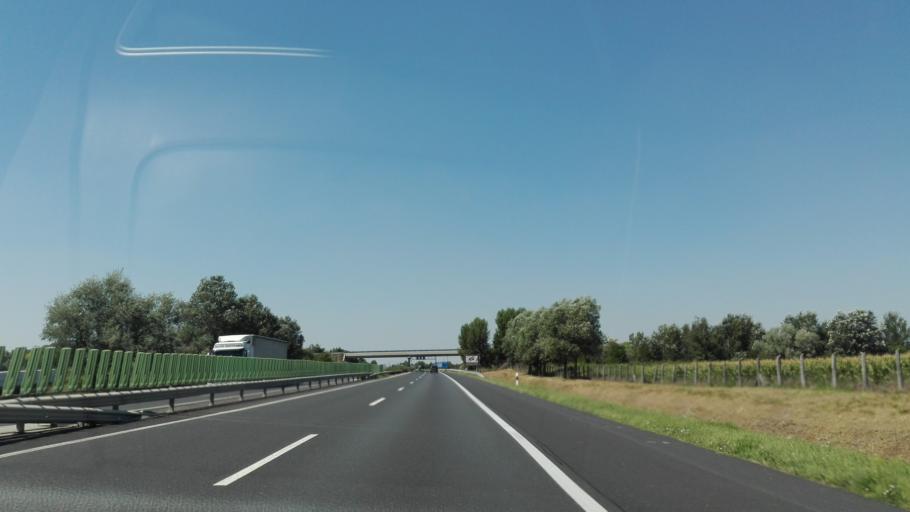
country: HU
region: Gyor-Moson-Sopron
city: Mosonmagyarovar
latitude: 47.8322
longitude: 17.2746
